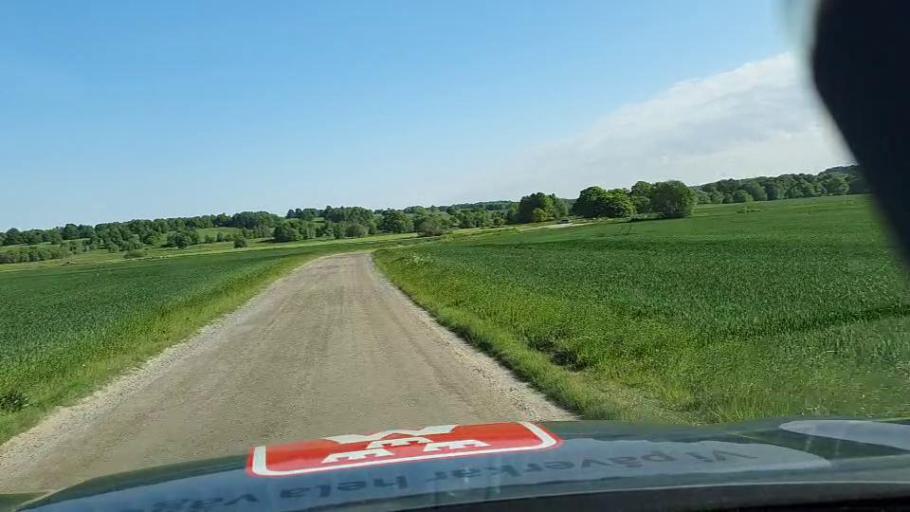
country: SE
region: Skane
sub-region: Hassleholms Kommun
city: Tormestorp
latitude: 56.1155
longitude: 13.7183
